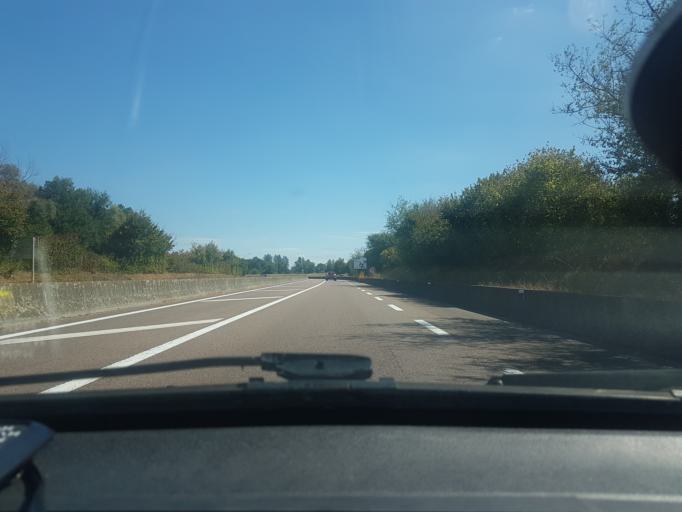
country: FR
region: Bourgogne
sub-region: Departement de la Cote-d'Or
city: Couternon
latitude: 47.3446
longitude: 5.1510
